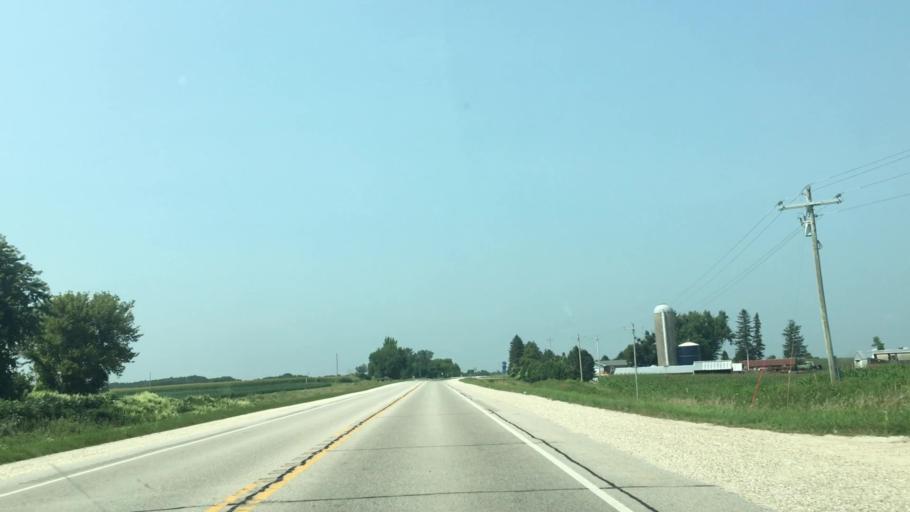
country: US
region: Iowa
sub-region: Winneshiek County
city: Decorah
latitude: 43.2009
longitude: -91.8762
